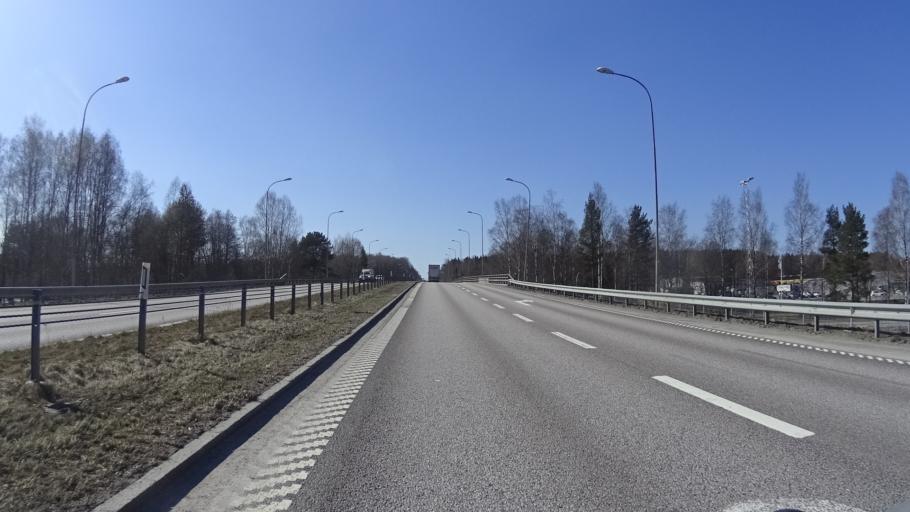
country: SE
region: OErebro
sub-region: Karlskoga Kommun
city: Karlskoga
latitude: 59.3235
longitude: 14.4842
